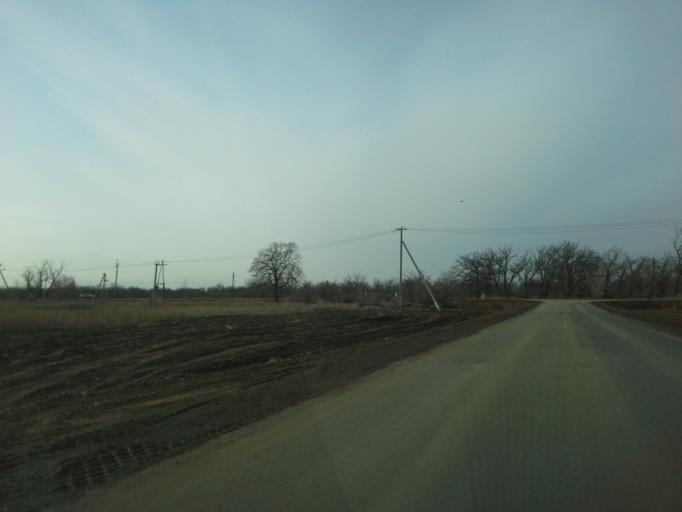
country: RU
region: Volgograd
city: Krasnoslobodsk
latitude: 48.6745
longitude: 44.5537
